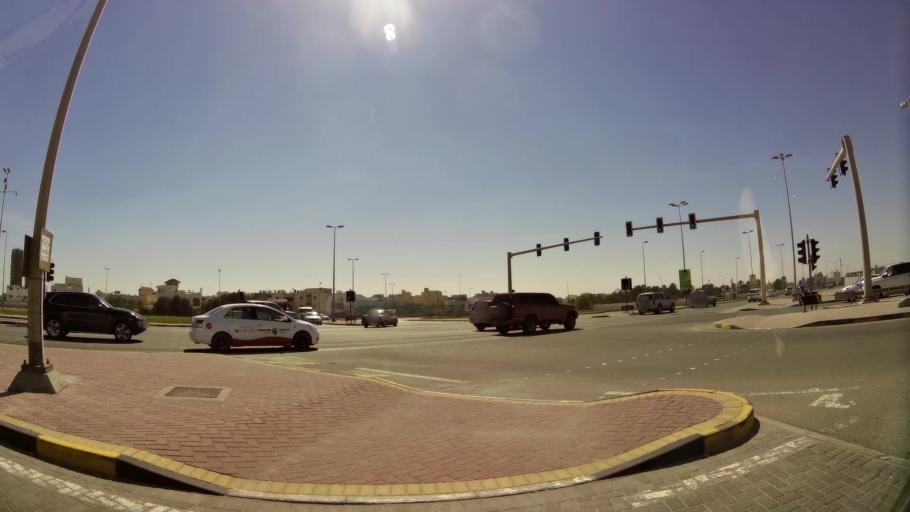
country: BH
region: Muharraq
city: Al Hadd
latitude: 26.2551
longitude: 50.6551
